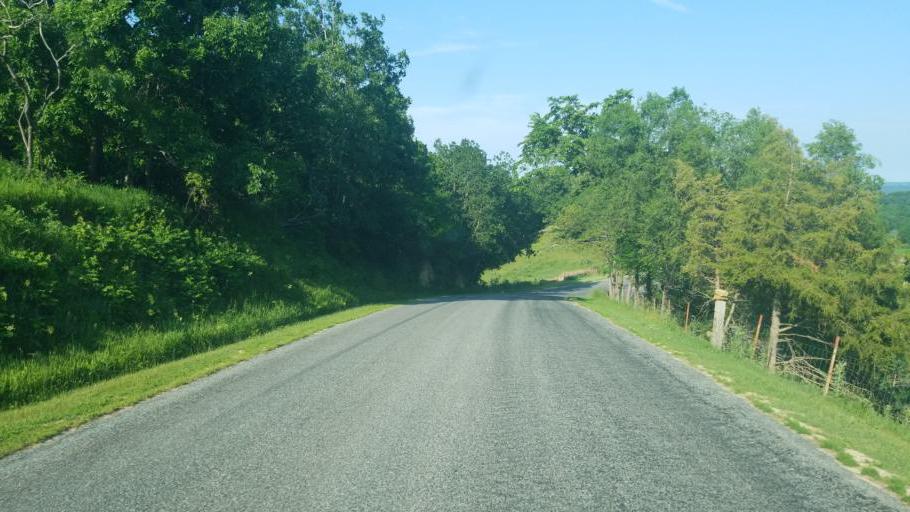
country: US
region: Wisconsin
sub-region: Vernon County
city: Hillsboro
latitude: 43.6820
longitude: -90.3718
